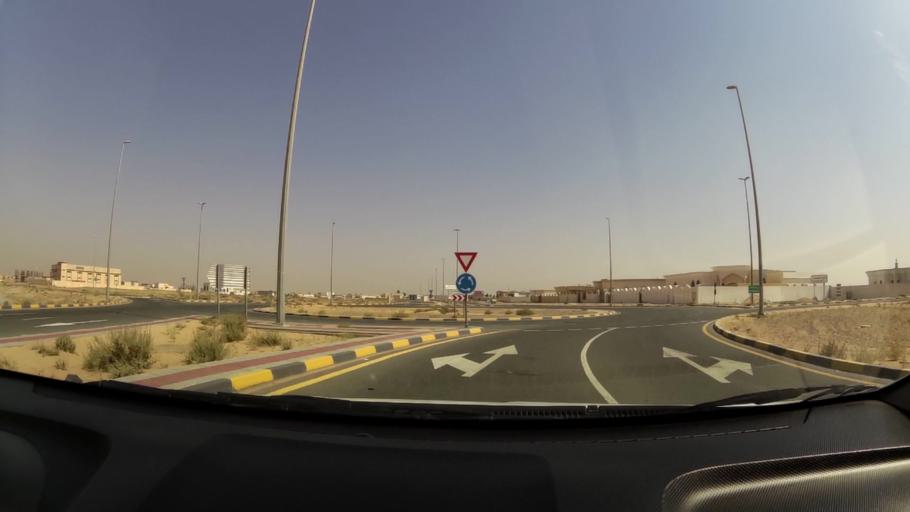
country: AE
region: Umm al Qaywayn
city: Umm al Qaywayn
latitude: 25.4792
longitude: 55.6040
